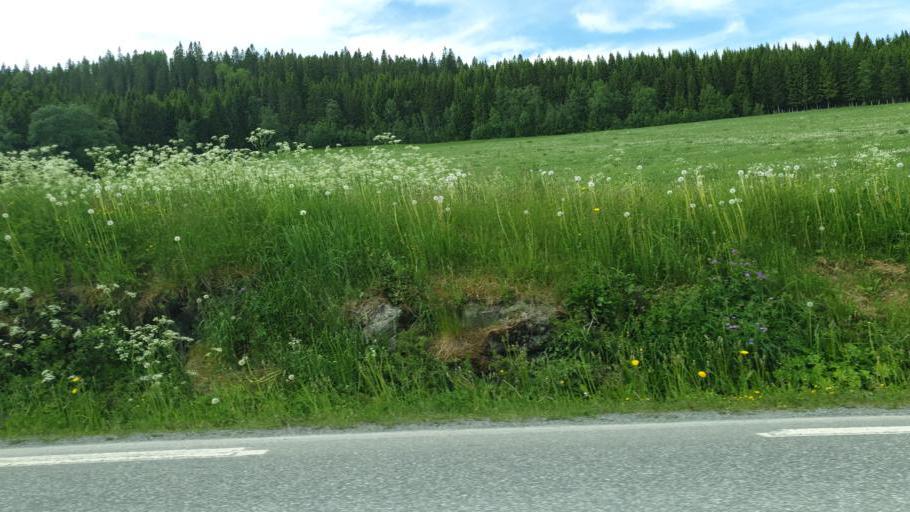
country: NO
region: Nord-Trondelag
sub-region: Leksvik
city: Leksvik
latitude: 63.6586
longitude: 10.6084
